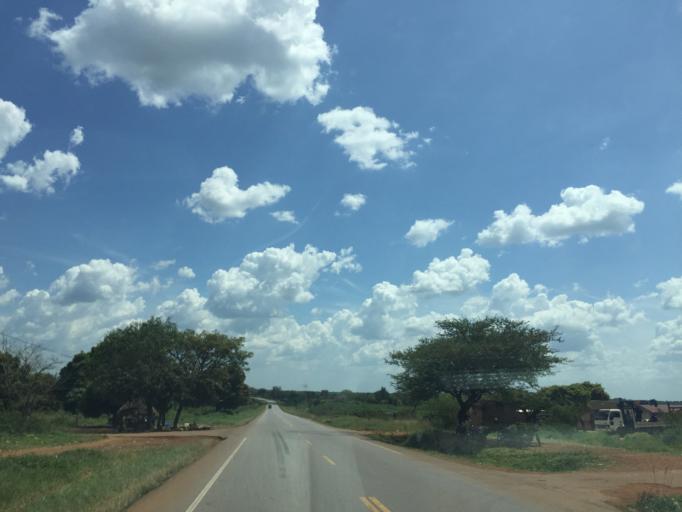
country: UG
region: Central Region
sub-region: Nakasongola District
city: Nakasongola
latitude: 1.3069
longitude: 32.4220
